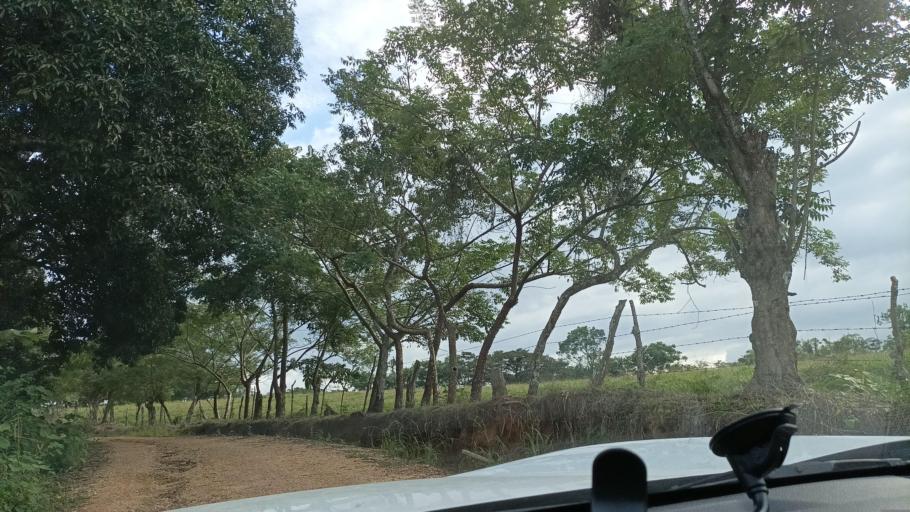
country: MX
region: Veracruz
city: Soconusco
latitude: 17.9448
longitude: -94.8828
